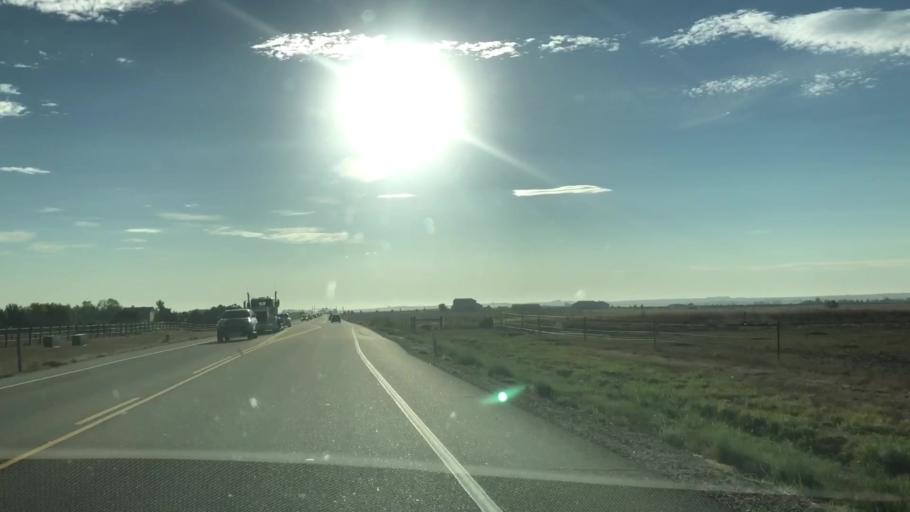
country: US
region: Colorado
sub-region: Weld County
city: Windsor
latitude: 40.4359
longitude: -104.9546
